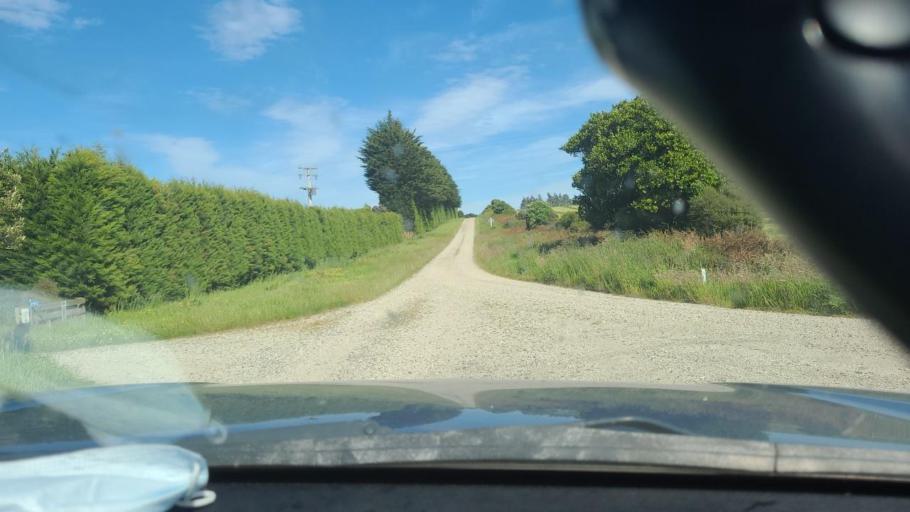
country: NZ
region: Southland
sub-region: Gore District
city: Gore
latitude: -46.4978
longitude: 168.8299
